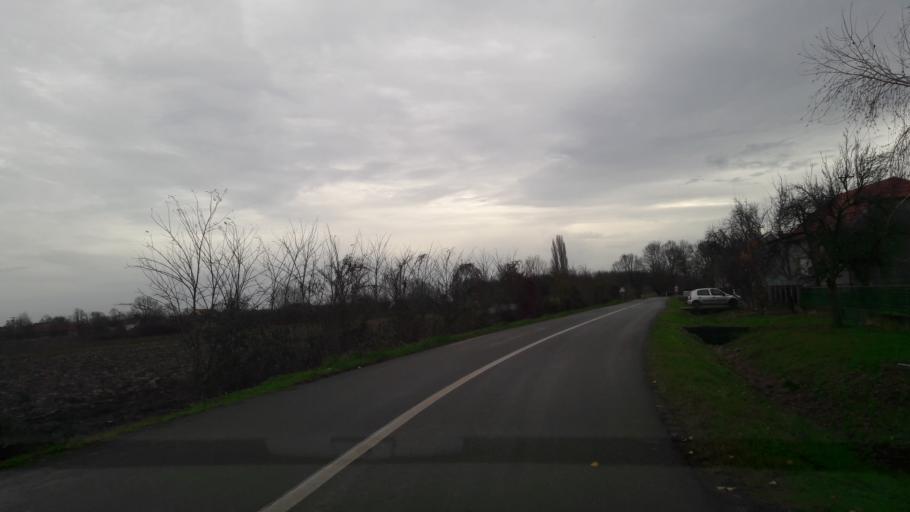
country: HR
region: Virovitick-Podravska
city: Zdenci
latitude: 45.6062
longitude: 18.0076
